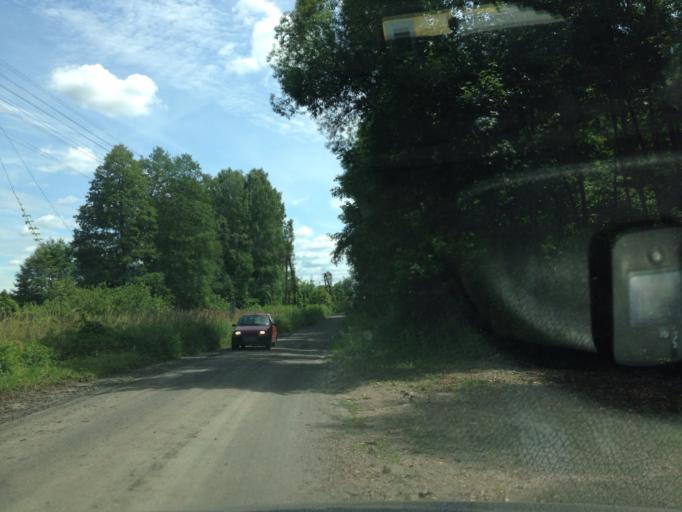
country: PL
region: Kujawsko-Pomorskie
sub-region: Powiat brodnicki
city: Bartniczka
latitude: 53.2657
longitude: 19.5814
